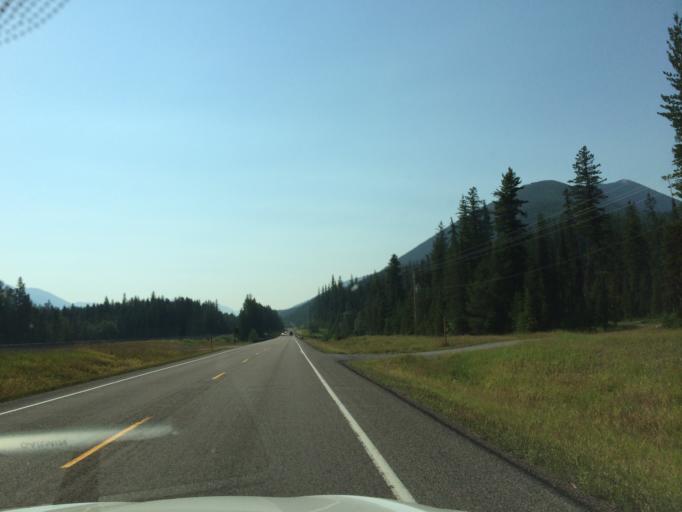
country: US
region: Montana
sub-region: Flathead County
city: Columbia Falls
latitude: 48.4014
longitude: -113.7150
